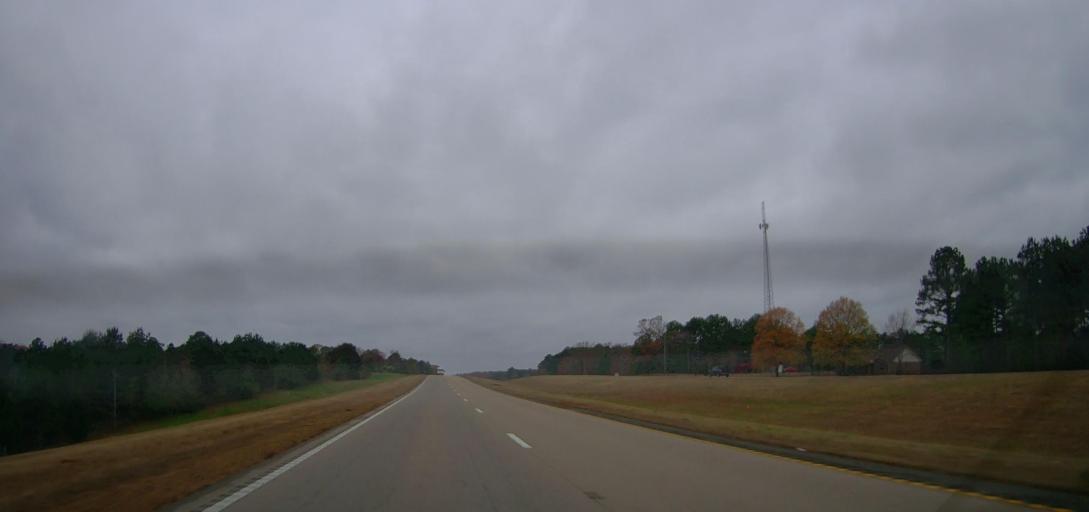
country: US
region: Mississippi
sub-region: Benton County
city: Ashland
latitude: 34.9533
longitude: -89.0132
